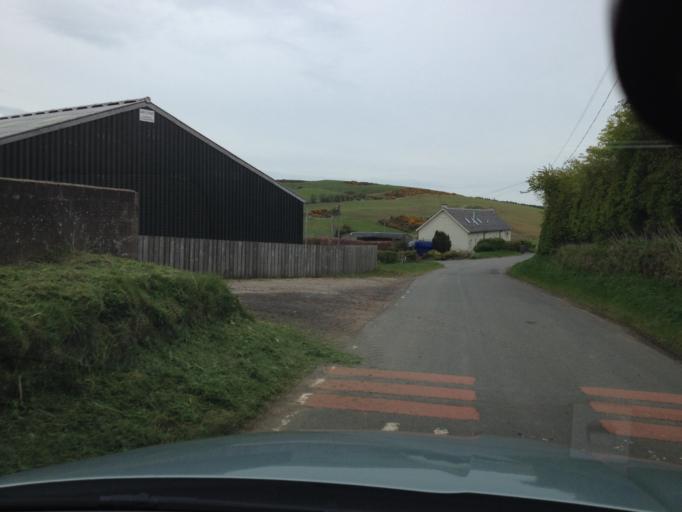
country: GB
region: Scotland
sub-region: West Lothian
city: Linlithgow
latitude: 55.9371
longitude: -3.5851
